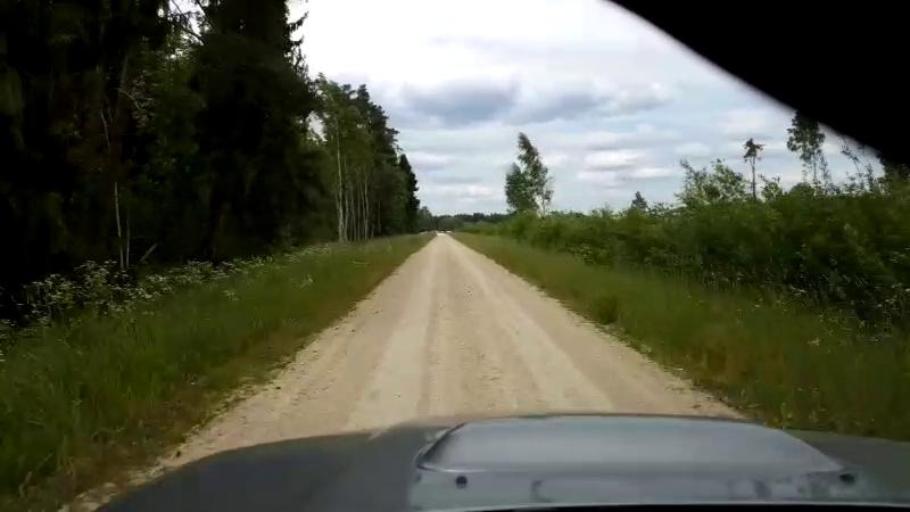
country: EE
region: Paernumaa
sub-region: Sauga vald
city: Sauga
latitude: 58.5086
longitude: 24.5807
